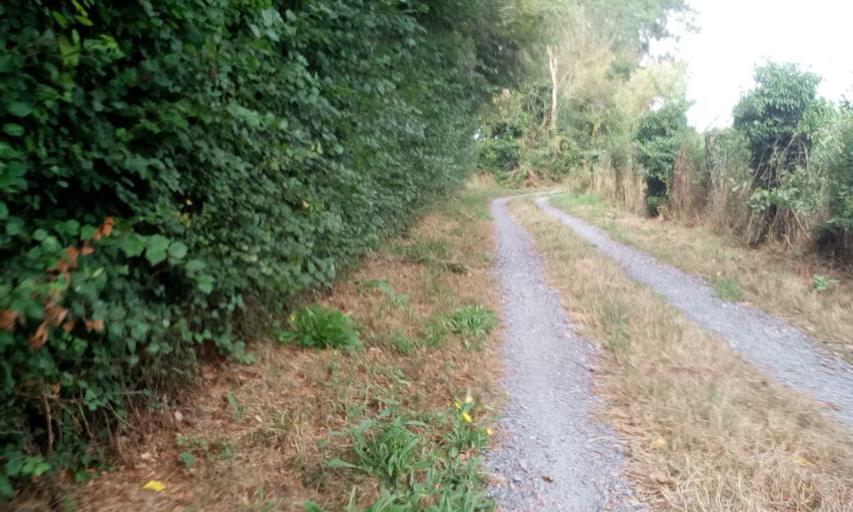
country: FR
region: Lower Normandy
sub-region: Departement du Calvados
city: Merville-Franceville-Plage
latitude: 49.2551
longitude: -0.2003
